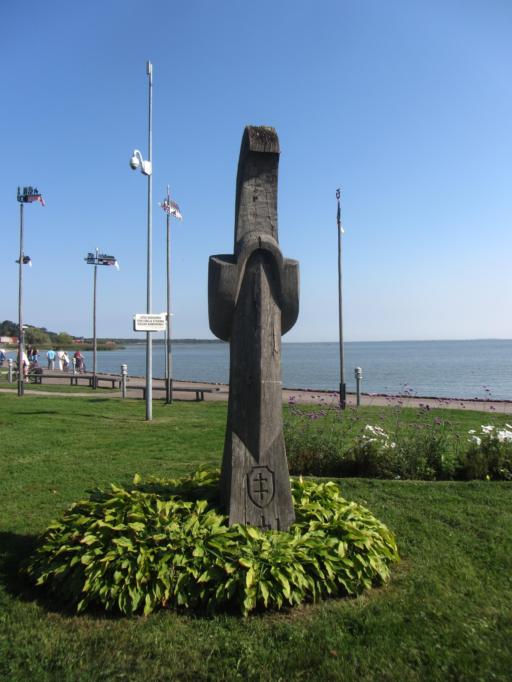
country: LT
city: Nida
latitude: 55.3061
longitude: 21.0072
